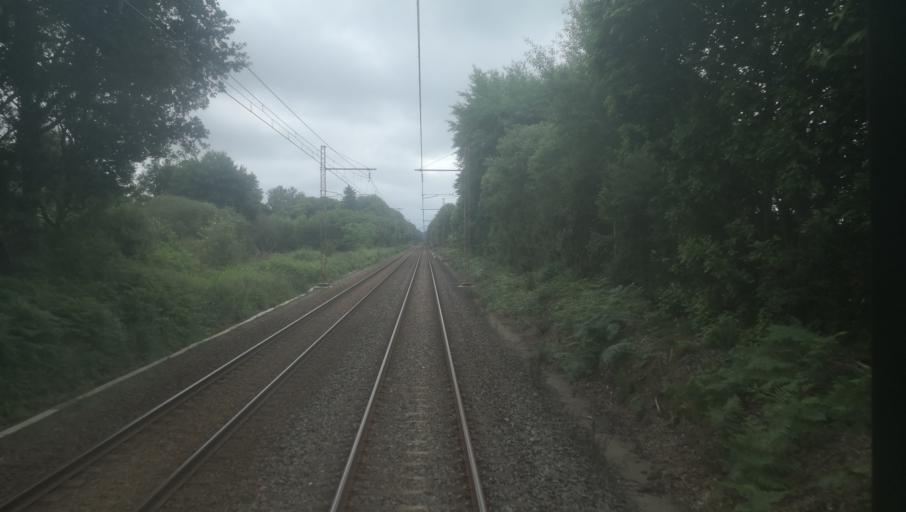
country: FR
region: Limousin
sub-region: Departement de la Haute-Vienne
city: Ambazac
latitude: 45.9591
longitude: 1.4266
